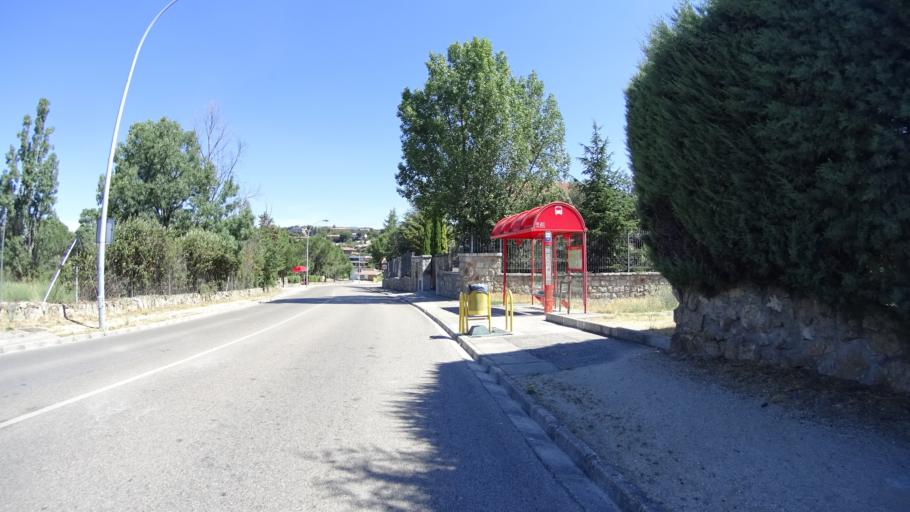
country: ES
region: Madrid
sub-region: Provincia de Madrid
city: Torrelodones
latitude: 40.6030
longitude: -3.9400
